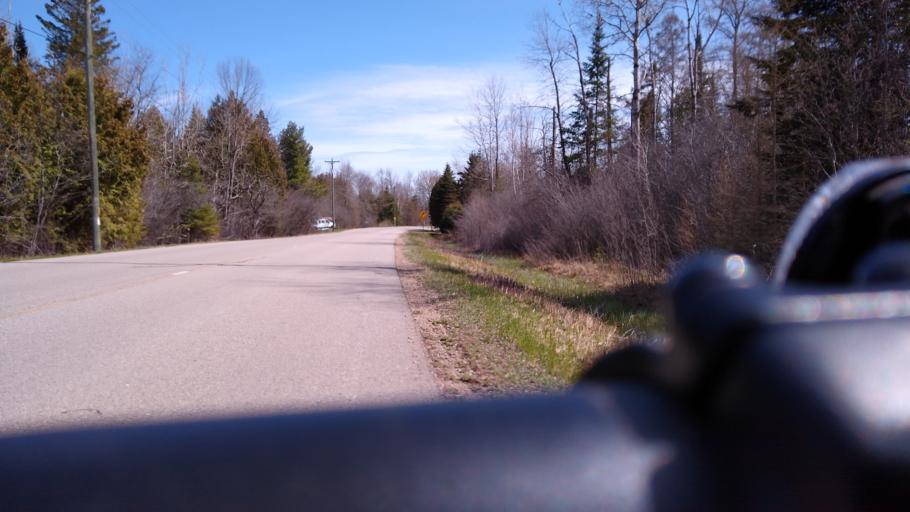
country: US
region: Michigan
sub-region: Delta County
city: Escanaba
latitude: 45.6825
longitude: -87.1457
